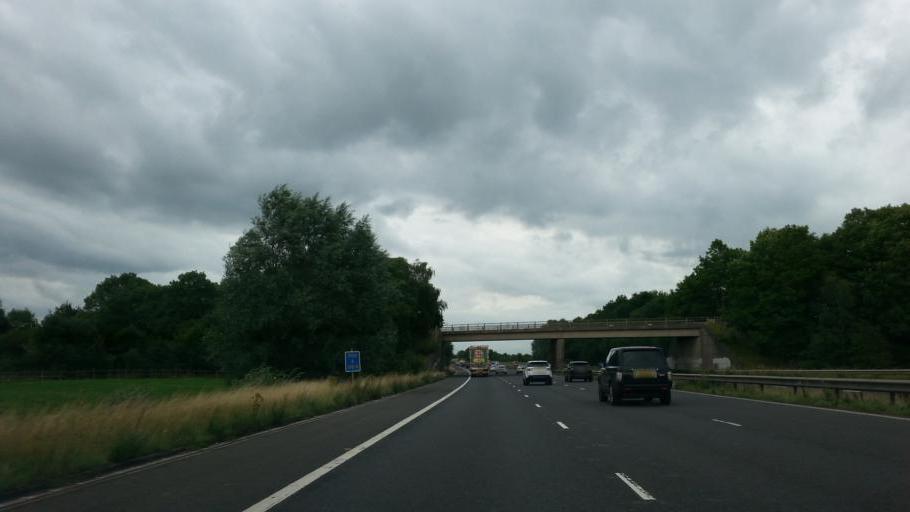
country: GB
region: England
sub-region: Leicestershire
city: Stoney Stanton
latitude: 52.5680
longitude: -1.2739
